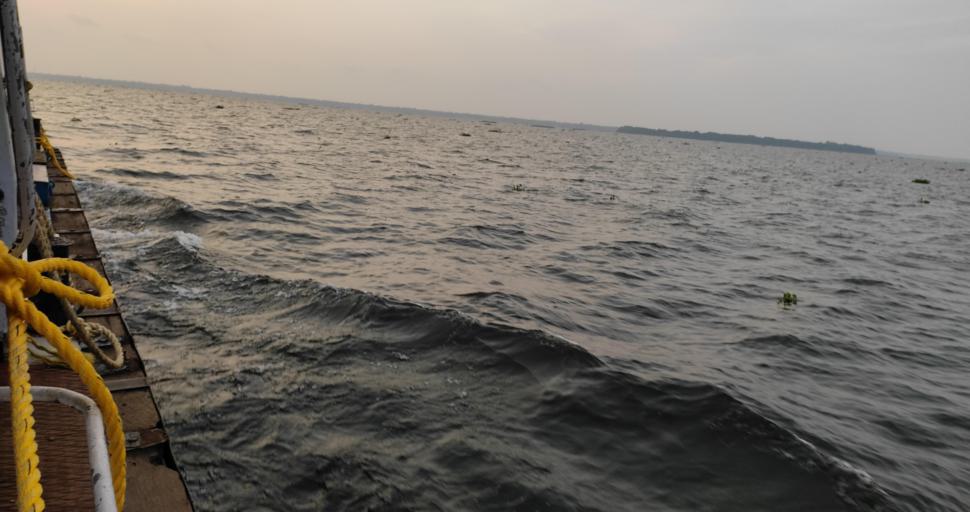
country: IN
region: Kerala
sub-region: Alappuzha
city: Shertallai
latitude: 9.6023
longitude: 76.3962
